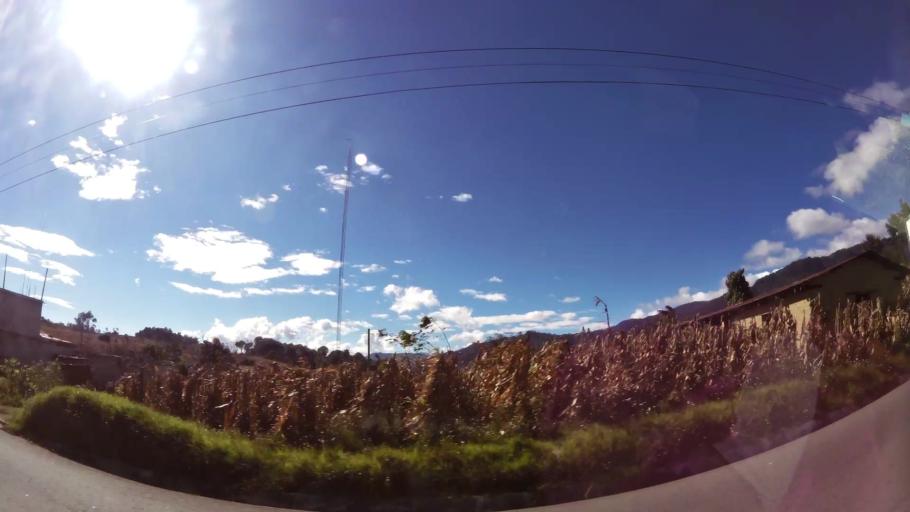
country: GT
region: Solola
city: Concepcion
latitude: 14.8190
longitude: -91.1788
